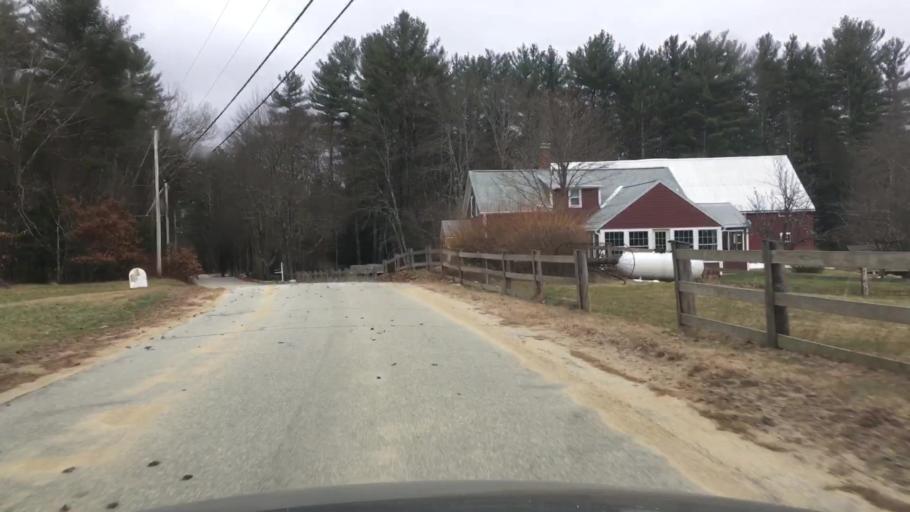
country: US
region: New Hampshire
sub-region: Hillsborough County
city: Mont Vernon
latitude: 42.9076
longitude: -71.6058
